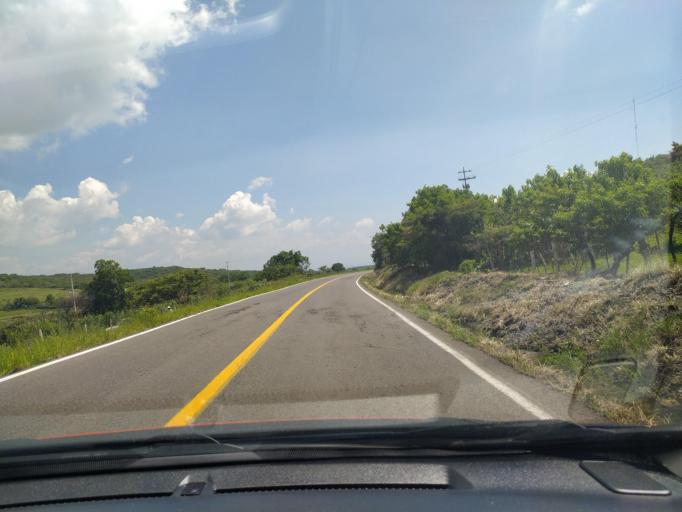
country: MX
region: Guanajuato
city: Ciudad Manuel Doblado
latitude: 20.5619
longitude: -101.9700
